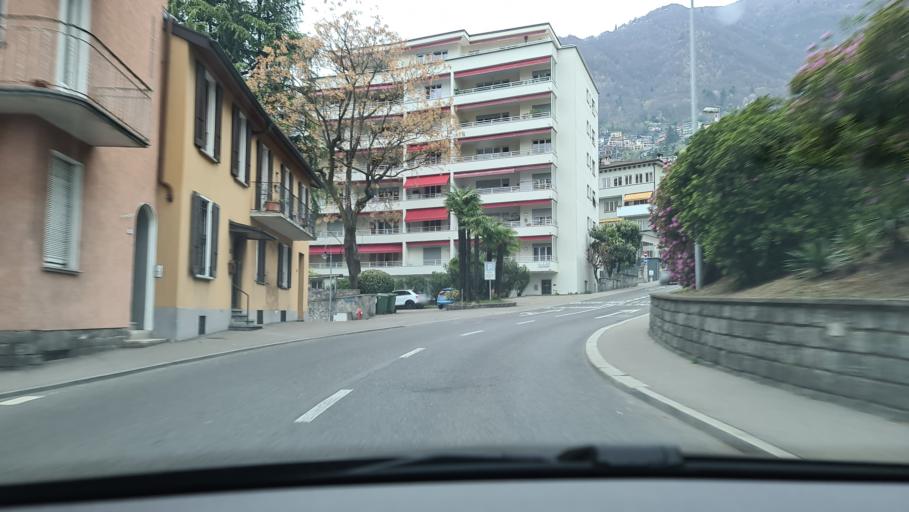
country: CH
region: Ticino
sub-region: Locarno District
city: Locarno
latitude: 46.1734
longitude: 8.8071
